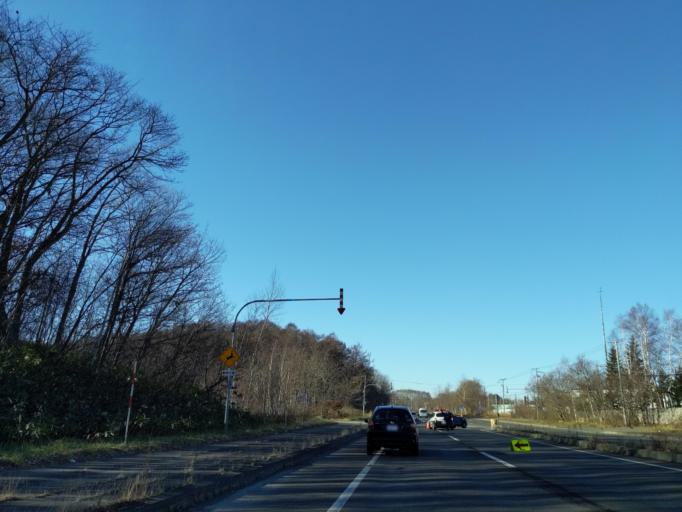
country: JP
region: Hokkaido
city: Kitahiroshima
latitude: 42.9335
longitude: 141.5257
